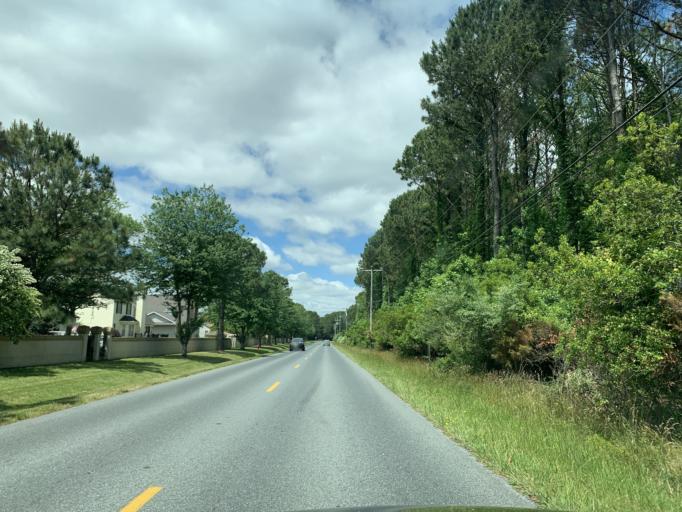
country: US
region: Maryland
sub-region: Worcester County
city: West Ocean City
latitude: 38.3491
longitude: -75.1128
